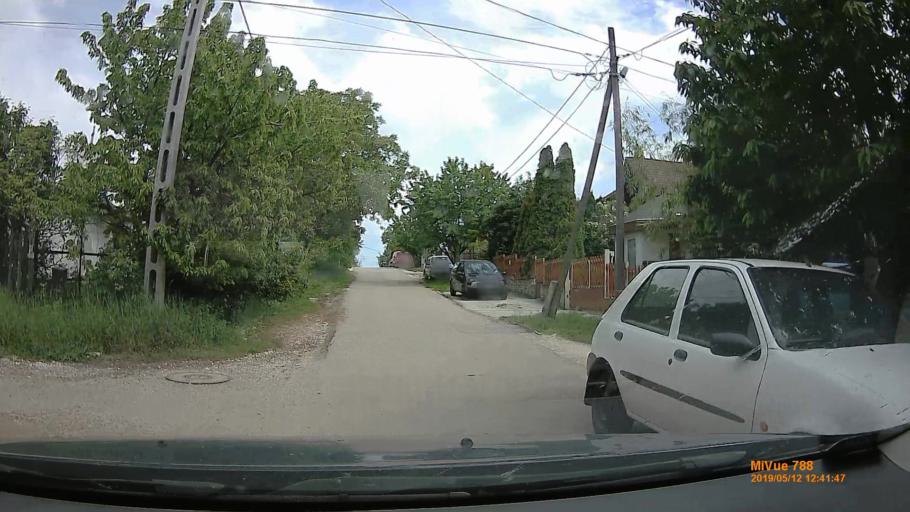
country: HU
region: Pest
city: Ecser
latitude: 47.4592
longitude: 19.3192
